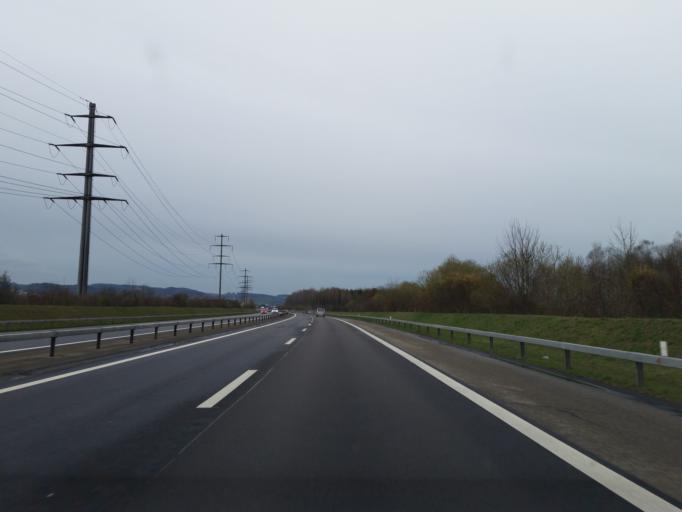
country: CH
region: Thurgau
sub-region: Frauenfeld District
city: Pfyn
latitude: 47.5832
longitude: 8.9322
